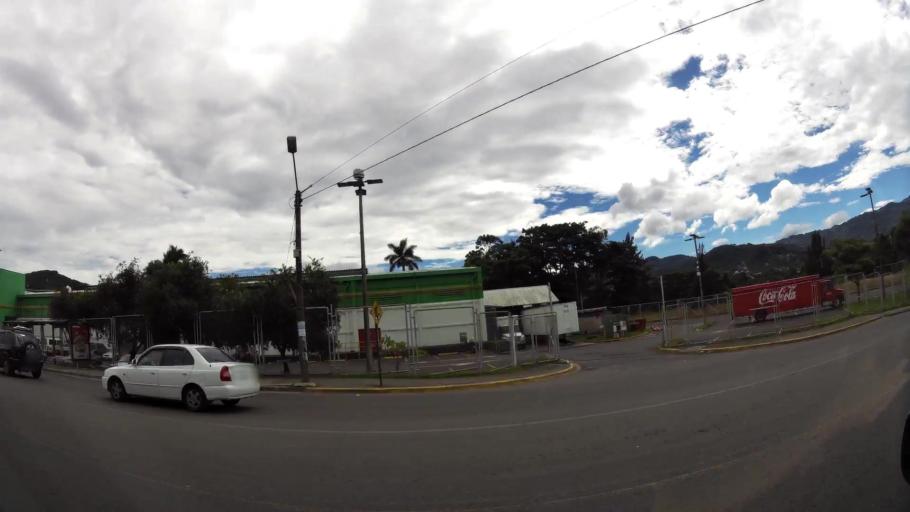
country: CR
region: San Jose
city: San Rafael Arriba
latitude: 9.8857
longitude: -84.0667
